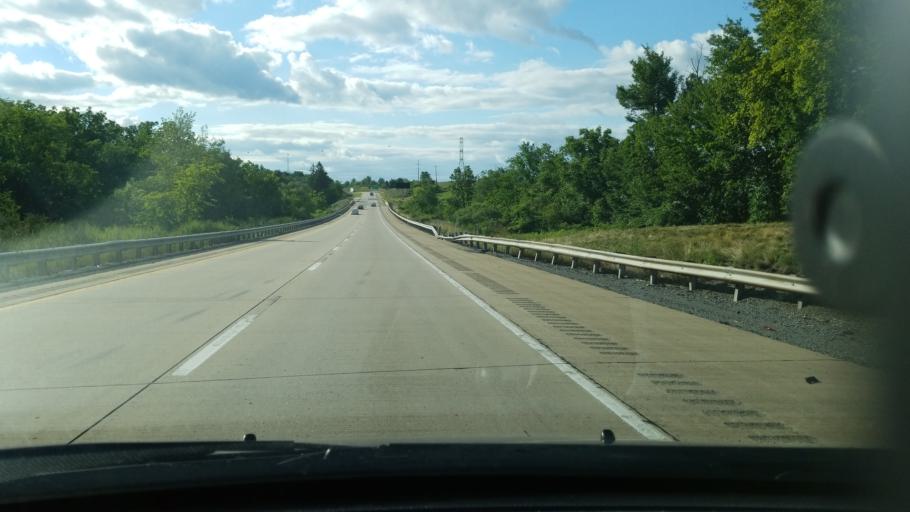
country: US
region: Pennsylvania
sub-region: Northumberland County
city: Milton
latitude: 40.9973
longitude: -76.7455
